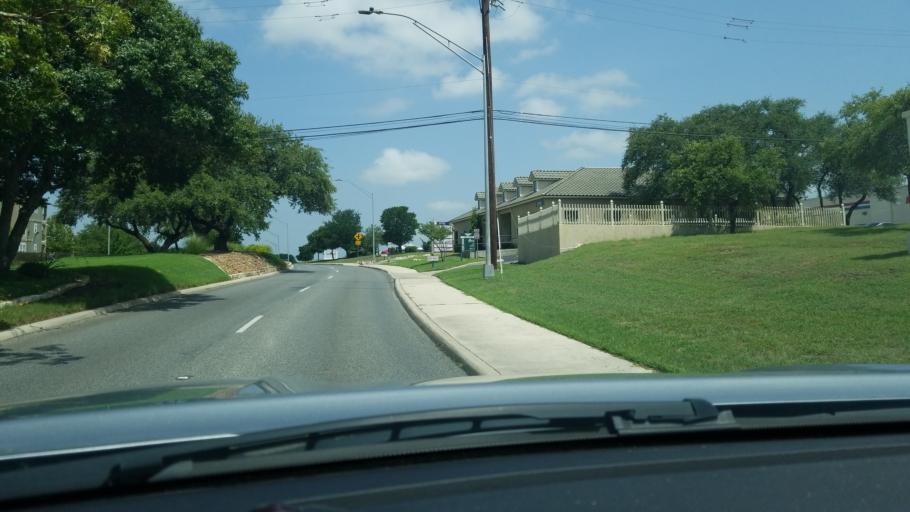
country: US
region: Texas
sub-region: Bexar County
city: Hollywood Park
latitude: 29.6444
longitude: -98.4914
